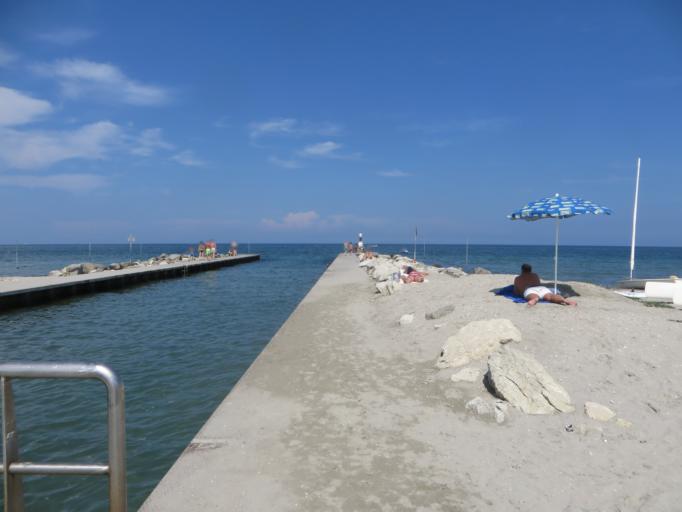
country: IT
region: Emilia-Romagna
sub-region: Provincia di Ravenna
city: Cervia
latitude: 44.2804
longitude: 12.3536
